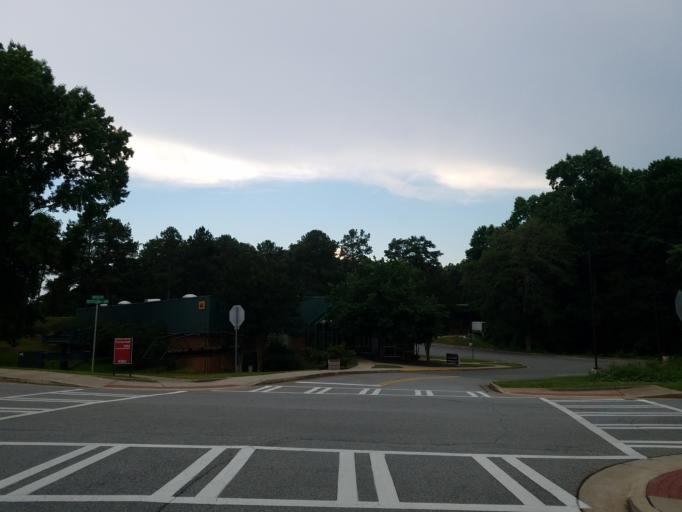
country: US
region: Georgia
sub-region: Cobb County
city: Fair Oaks
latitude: 33.9368
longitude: -84.5204
